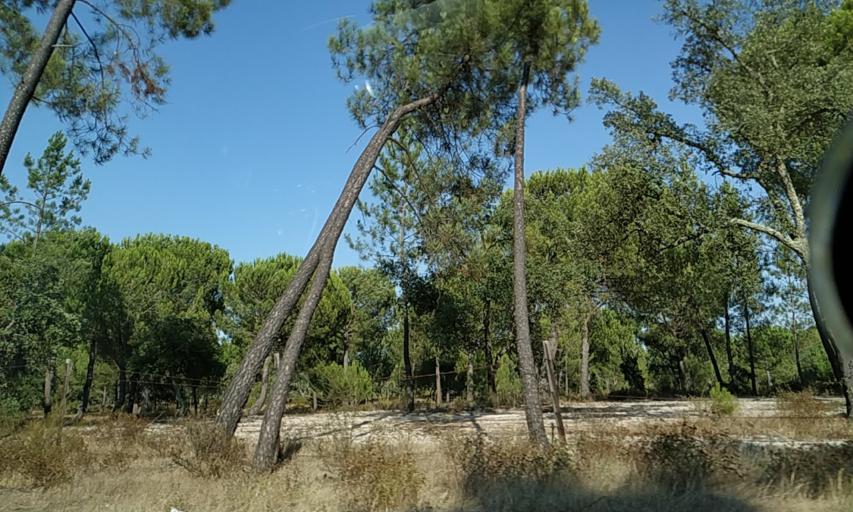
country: PT
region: Santarem
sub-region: Coruche
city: Coruche
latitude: 38.9058
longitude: -8.5273
